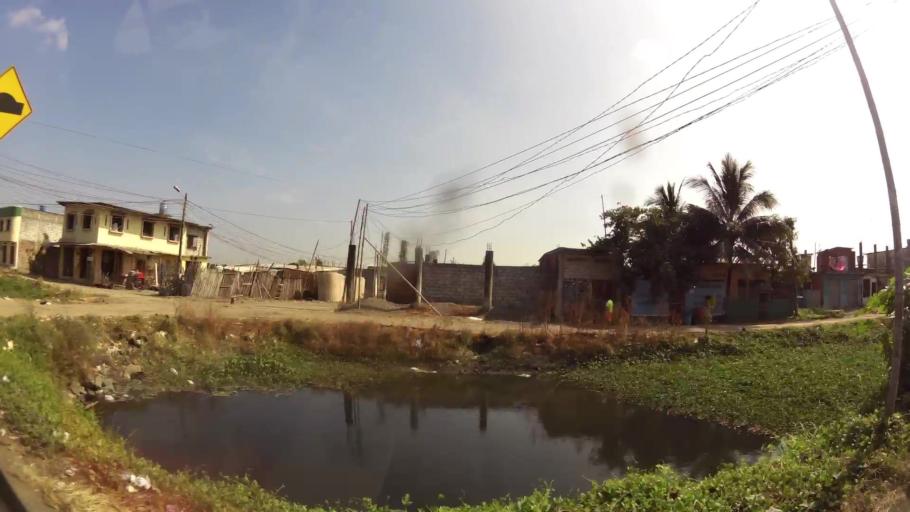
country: EC
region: Guayas
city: Eloy Alfaro
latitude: -2.1656
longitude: -79.7963
